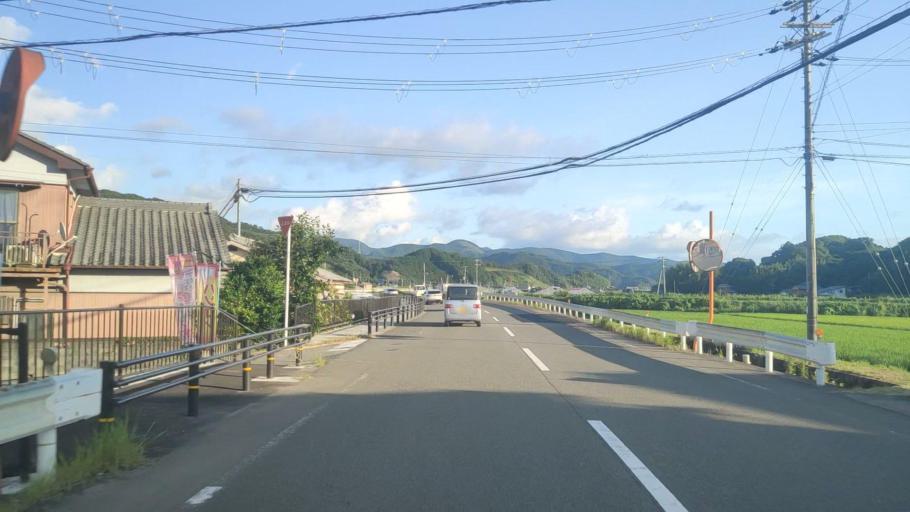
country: JP
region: Wakayama
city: Tanabe
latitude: 33.7190
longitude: 135.4459
